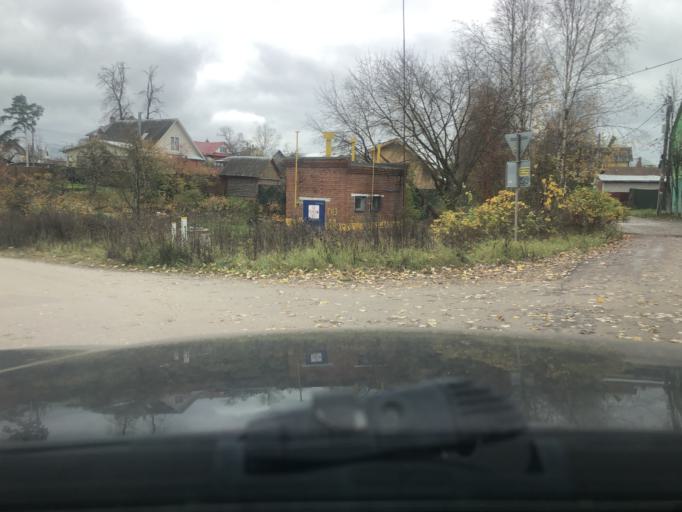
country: RU
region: Moskovskaya
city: Sergiyev Posad
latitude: 56.3110
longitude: 38.1169
